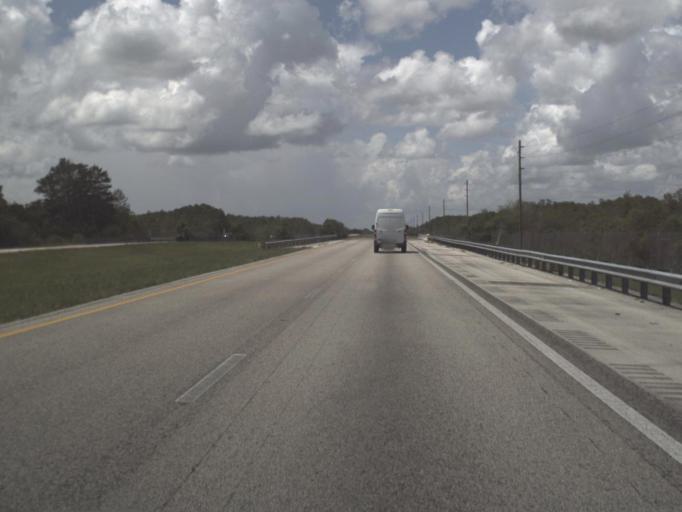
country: US
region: Florida
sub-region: Broward County
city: Weston
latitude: 26.1722
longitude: -80.9133
